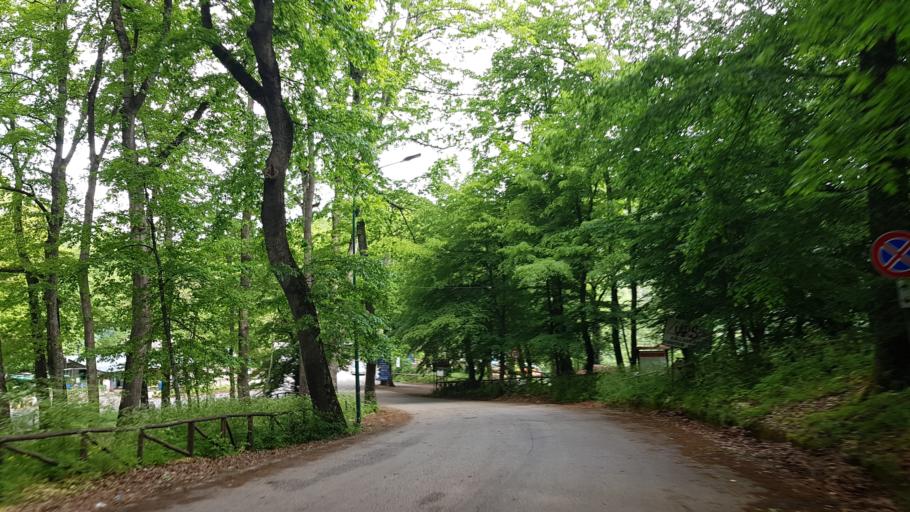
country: IT
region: Basilicate
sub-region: Provincia di Potenza
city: Rionero in Vulture
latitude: 40.9299
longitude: 15.6123
